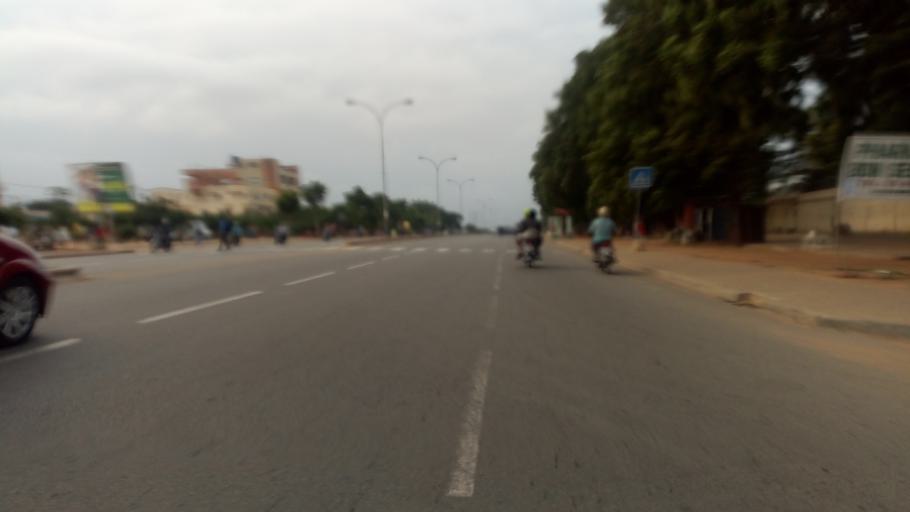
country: TG
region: Maritime
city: Lome
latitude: 6.1535
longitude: 1.2015
